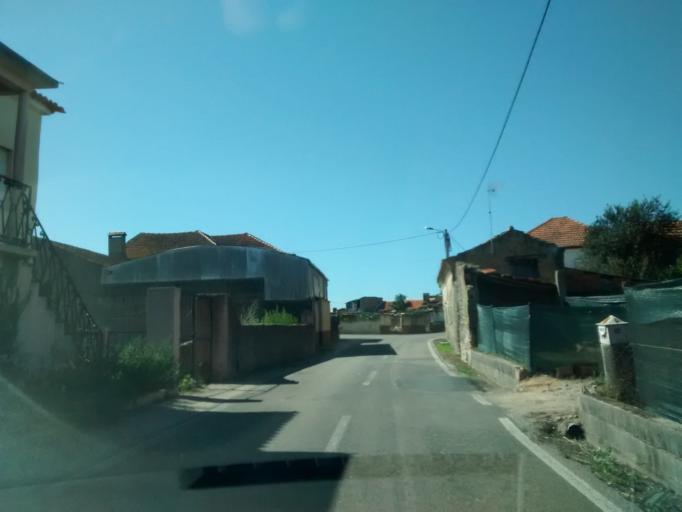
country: PT
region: Aveiro
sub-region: Anadia
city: Sangalhos
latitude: 40.4444
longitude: -8.5058
